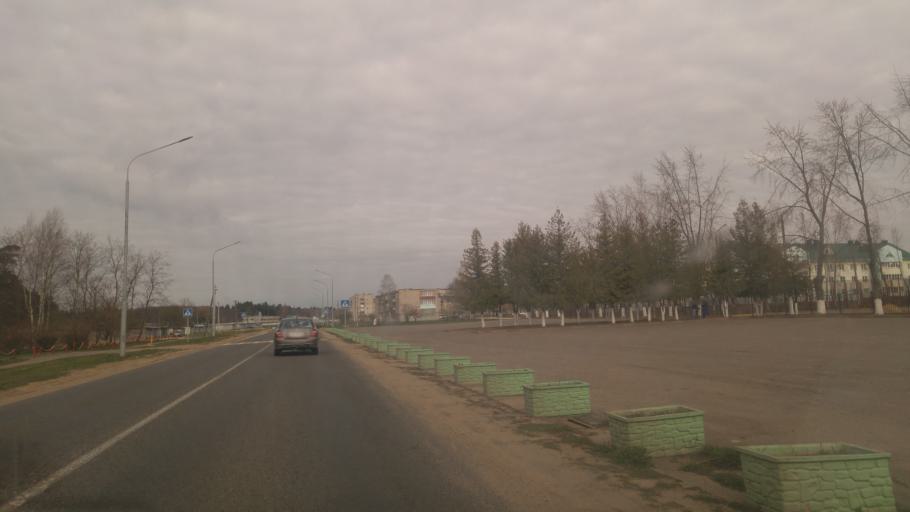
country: BY
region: Minsk
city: Chervyen'
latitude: 53.6999
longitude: 28.4171
